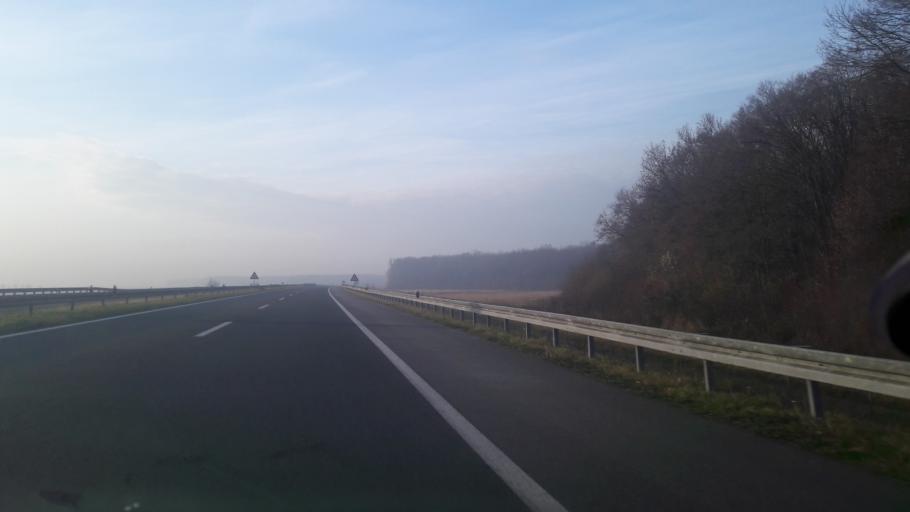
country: HR
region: Osjecko-Baranjska
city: Vuka
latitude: 45.4933
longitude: 18.5011
